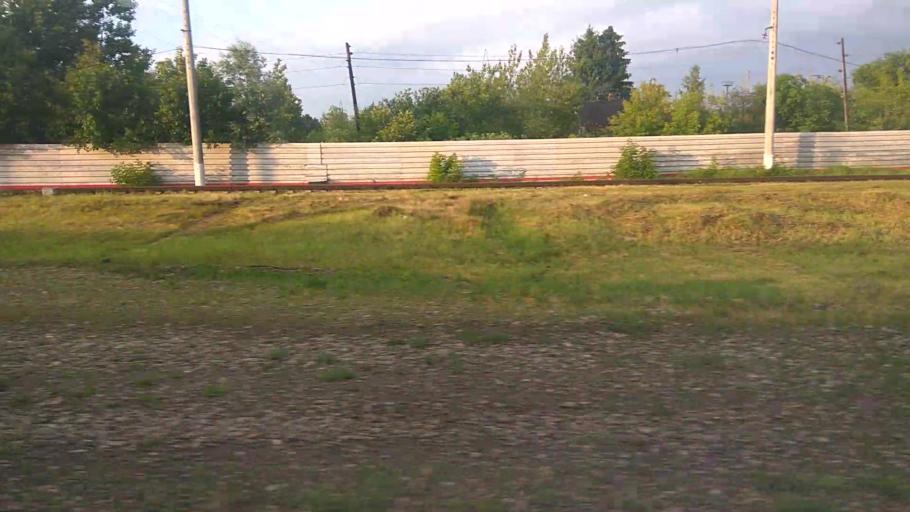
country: RU
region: Moskovskaya
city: Stupino
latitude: 54.9054
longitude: 38.0822
